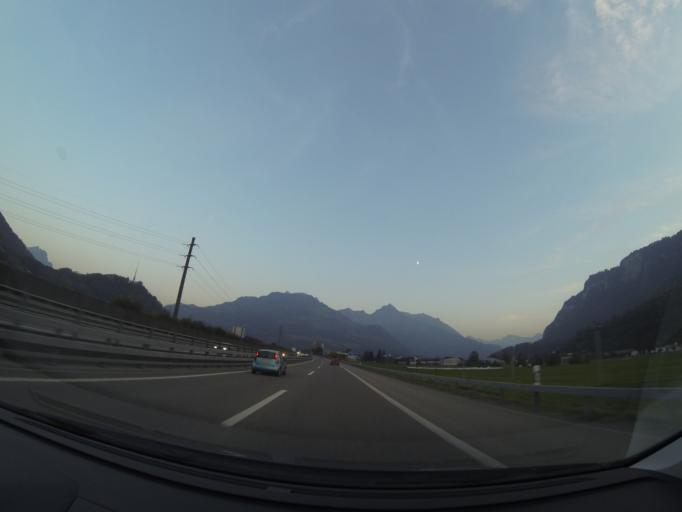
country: CH
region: Glarus
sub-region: Glarus
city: Niederurnen
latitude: 47.1347
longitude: 9.0539
